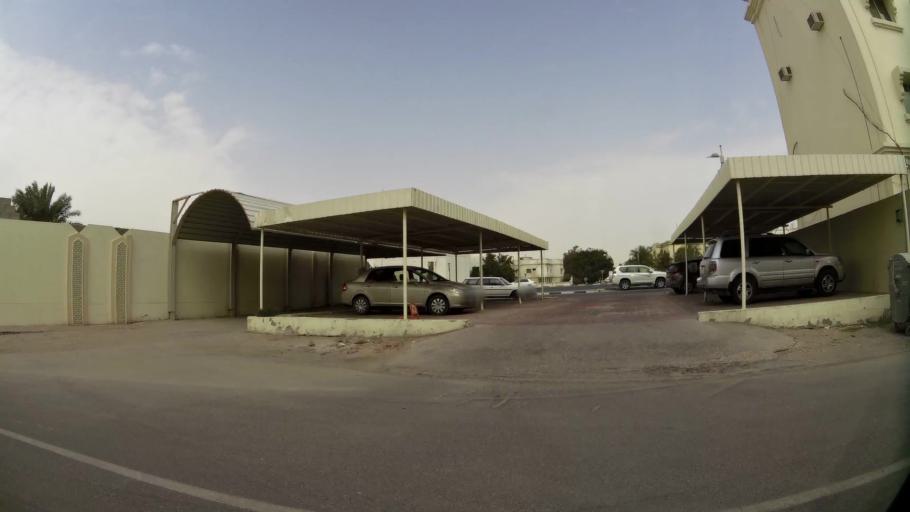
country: QA
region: Baladiyat ad Dawhah
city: Doha
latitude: 25.3096
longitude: 51.4951
